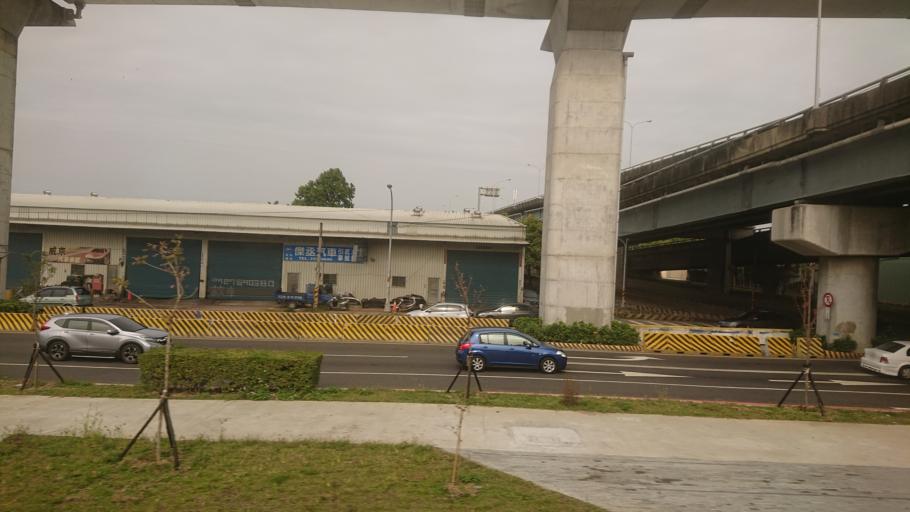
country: TW
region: Taiwan
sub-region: Taichung City
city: Taichung
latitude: 24.1150
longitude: 120.6419
